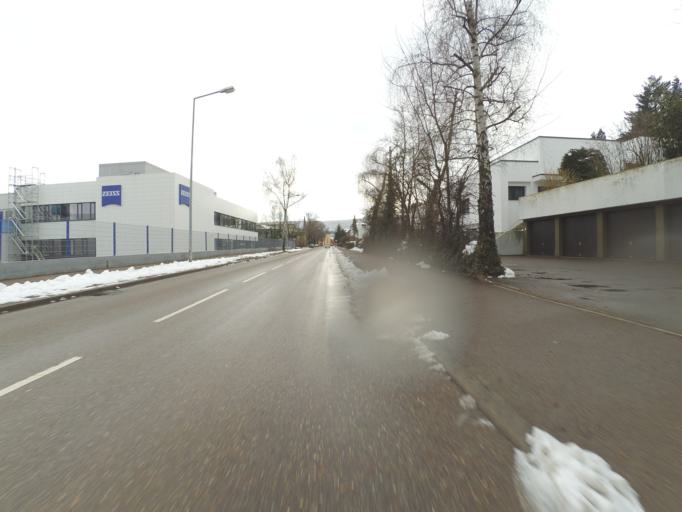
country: DE
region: Baden-Wuerttemberg
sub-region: Regierungsbezirk Stuttgart
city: Aalen
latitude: 48.8430
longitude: 10.0884
